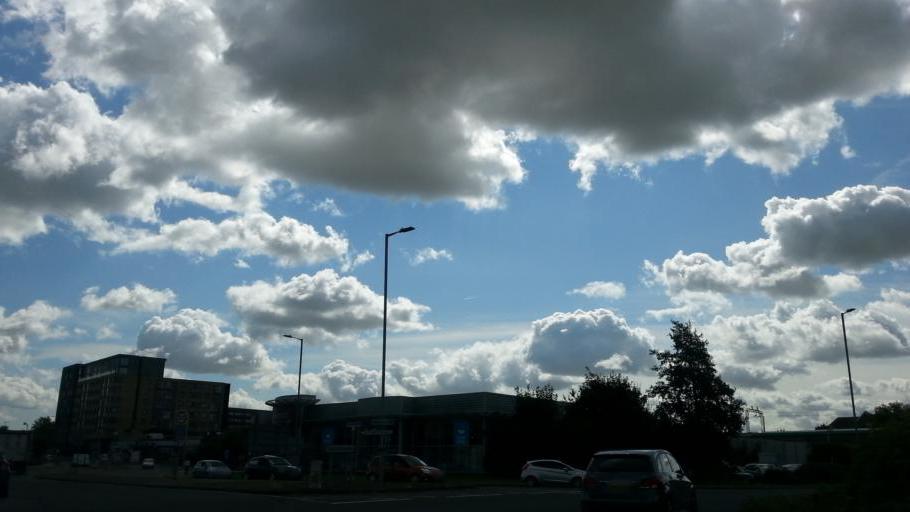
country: GB
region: England
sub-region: Essex
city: Basildon
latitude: 51.5694
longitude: 0.4523
